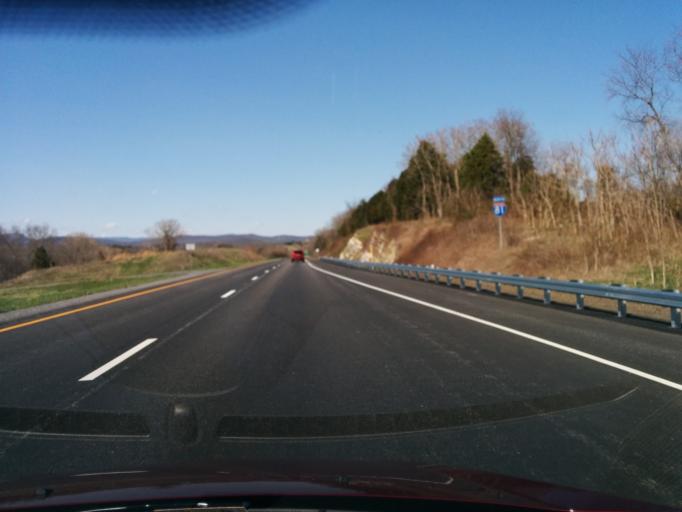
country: US
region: Virginia
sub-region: Rockbridge County
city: East Lexington
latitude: 37.7638
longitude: -79.4061
